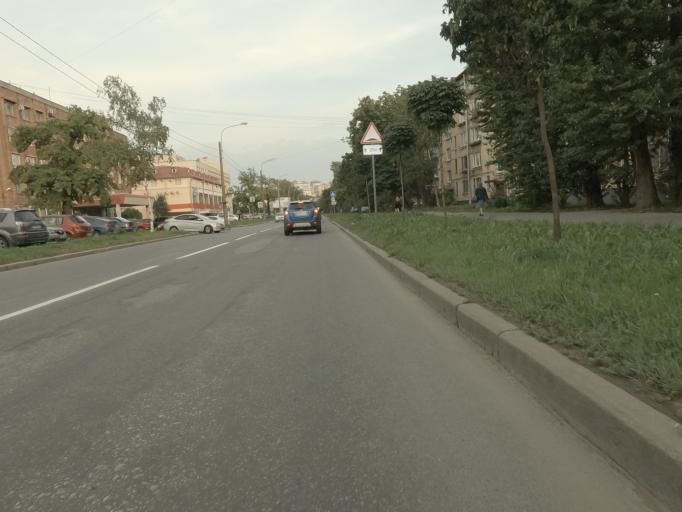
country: RU
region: St.-Petersburg
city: Dachnoye
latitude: 59.8556
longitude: 30.2625
